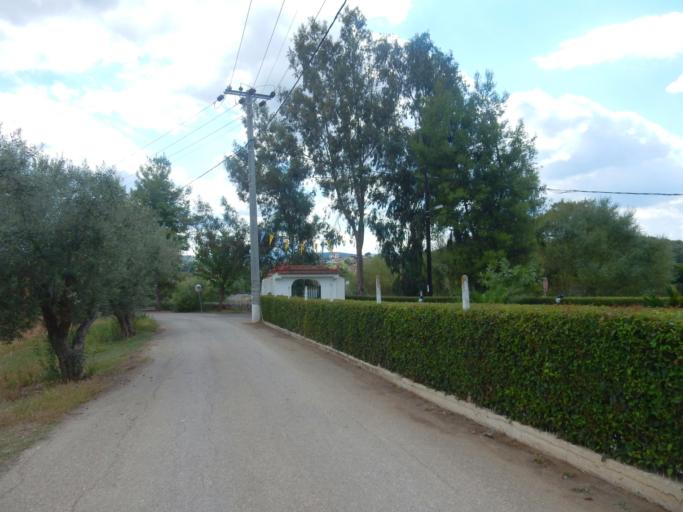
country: GR
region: Attica
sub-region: Nomarchia Anatolikis Attikis
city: Khalkoutsion
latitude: 38.3263
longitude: 23.7522
